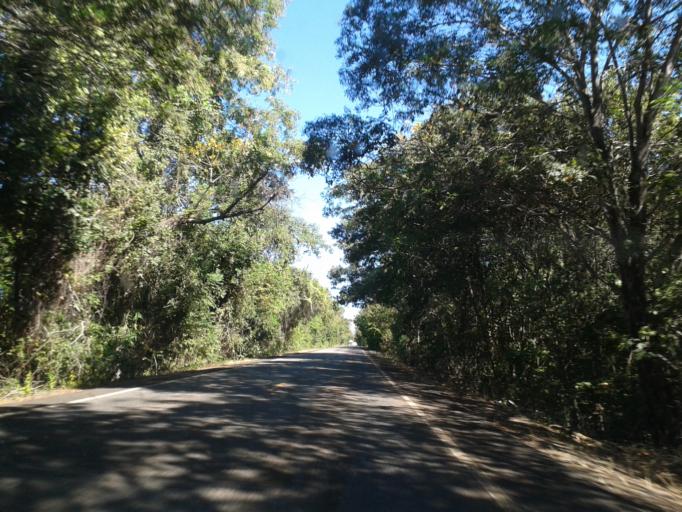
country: BR
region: Goias
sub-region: Crixas
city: Crixas
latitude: -14.0141
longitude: -50.3261
